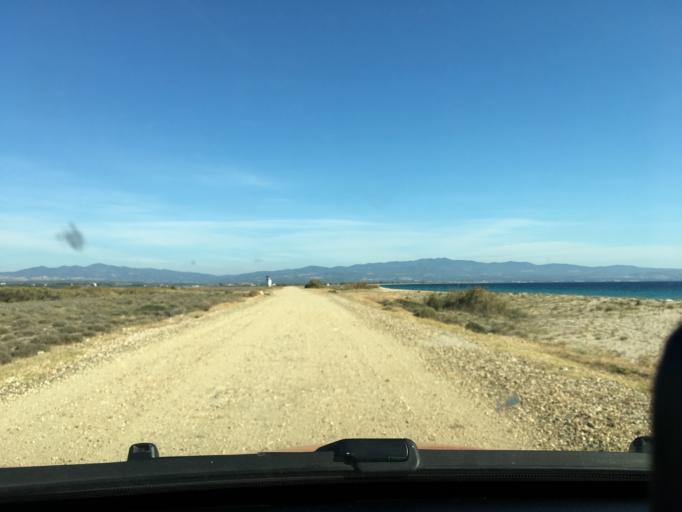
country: GR
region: Central Macedonia
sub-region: Nomos Chalkidikis
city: Nea Potidhaia
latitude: 40.2142
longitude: 23.3317
